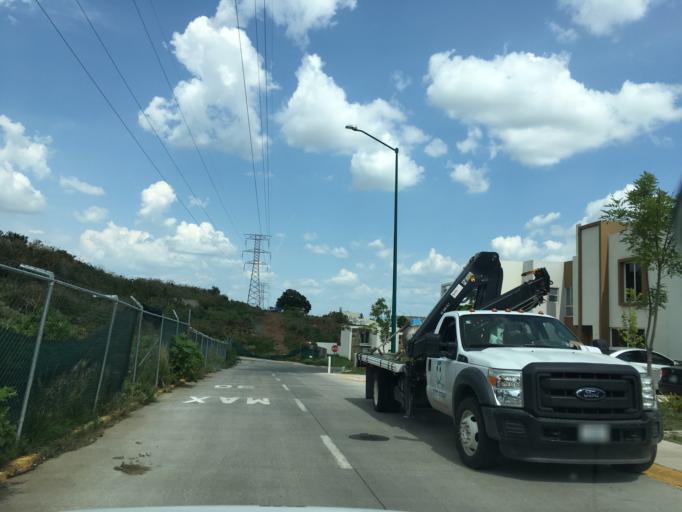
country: MX
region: Jalisco
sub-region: Tlajomulco de Zuniga
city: Altus Bosques
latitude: 20.5865
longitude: -103.3656
